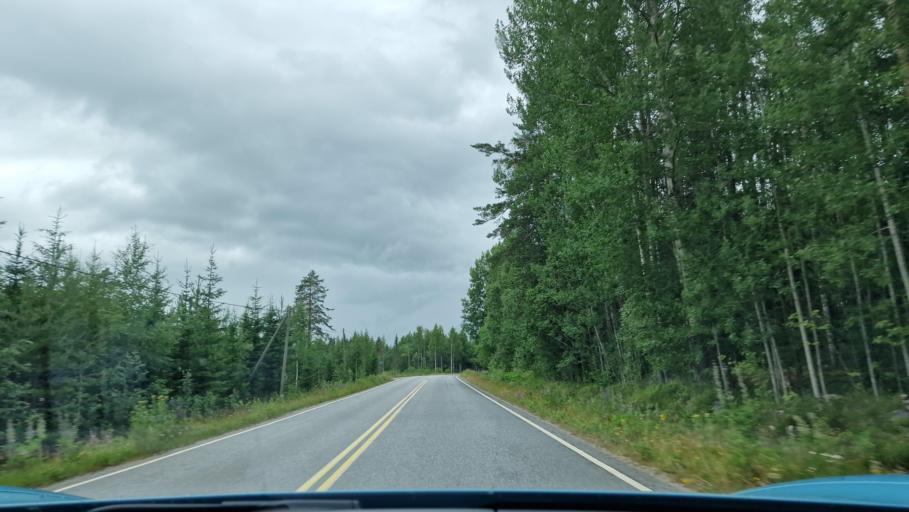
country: FI
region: Southern Ostrobothnia
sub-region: Jaerviseutu
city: Soini
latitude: 62.7596
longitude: 24.3901
